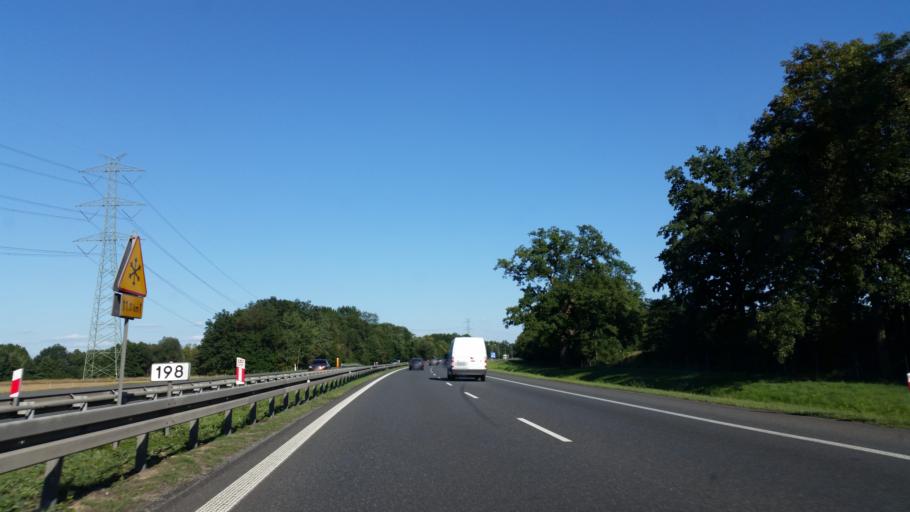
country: PL
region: Opole Voivodeship
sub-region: Powiat brzeski
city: Grodkow
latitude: 50.7690
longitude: 17.3995
